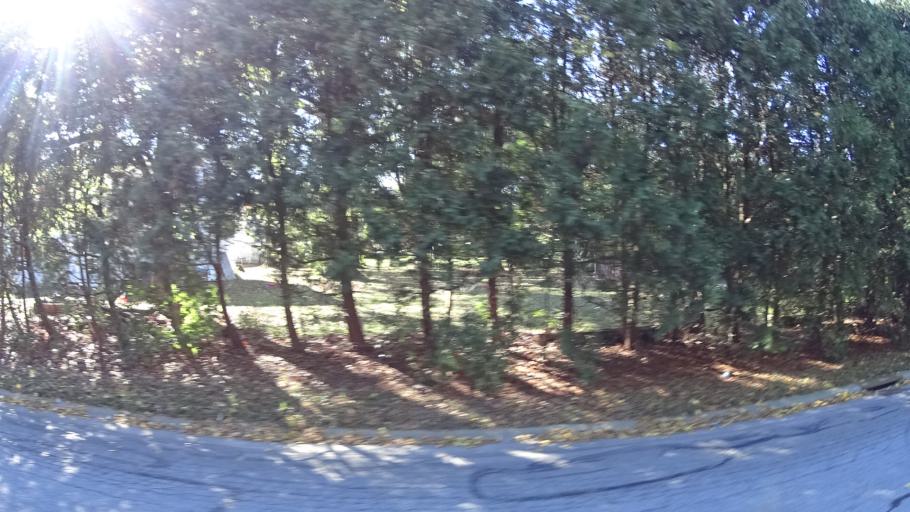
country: US
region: Ohio
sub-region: Lorain County
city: Oberlin
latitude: 41.2824
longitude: -82.2209
